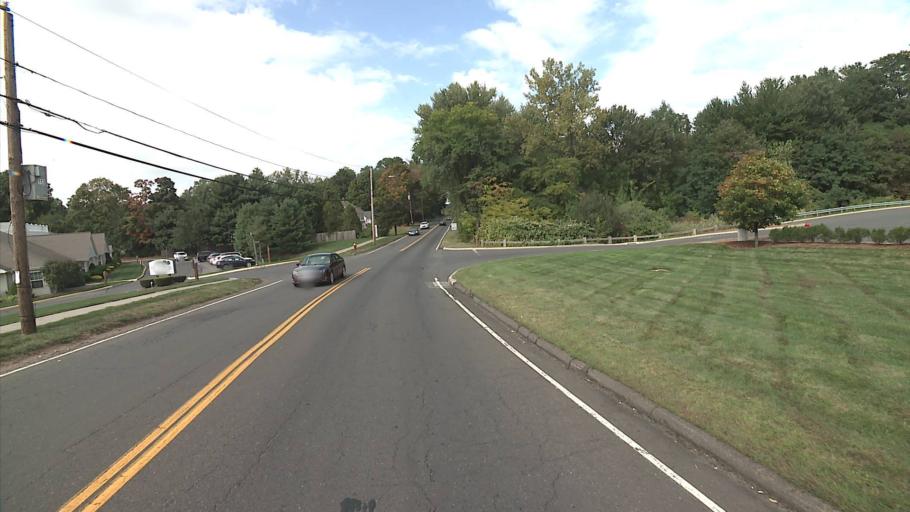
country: US
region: Connecticut
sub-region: Hartford County
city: Newington
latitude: 41.6711
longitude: -72.7186
